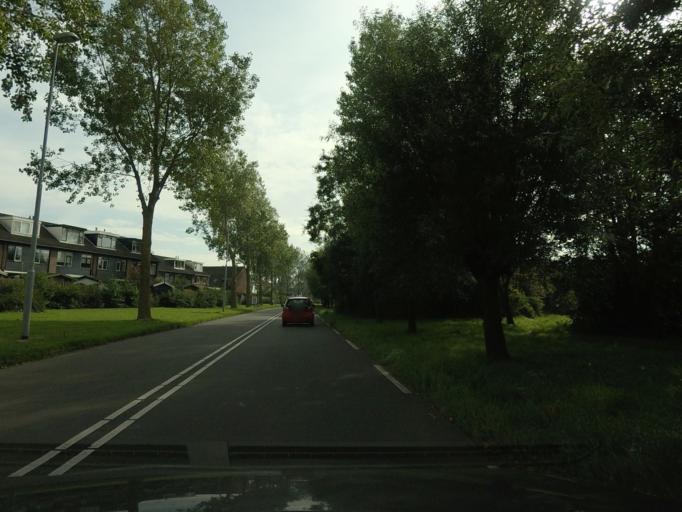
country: NL
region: North Holland
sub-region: Gemeente Den Helder
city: Den Helder
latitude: 52.8901
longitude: 4.7375
